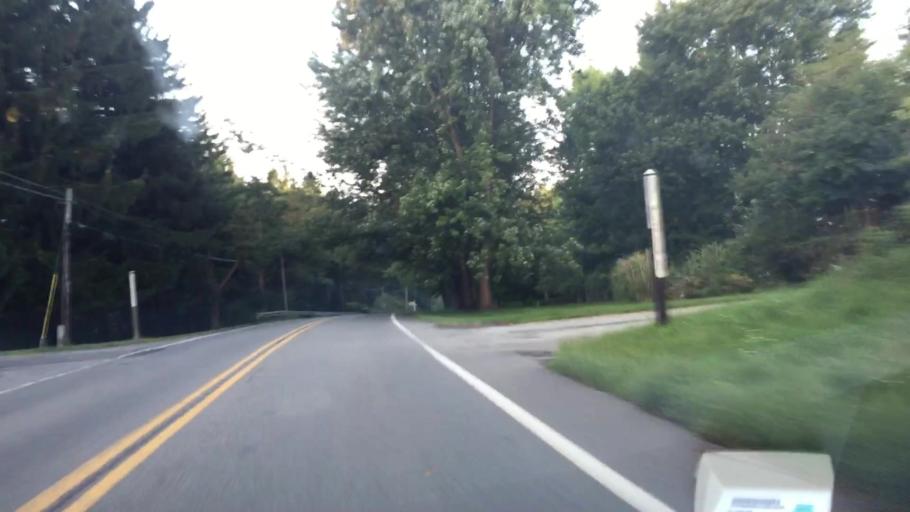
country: US
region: Pennsylvania
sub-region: Allegheny County
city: Franklin Park
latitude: 40.5820
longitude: -80.1056
